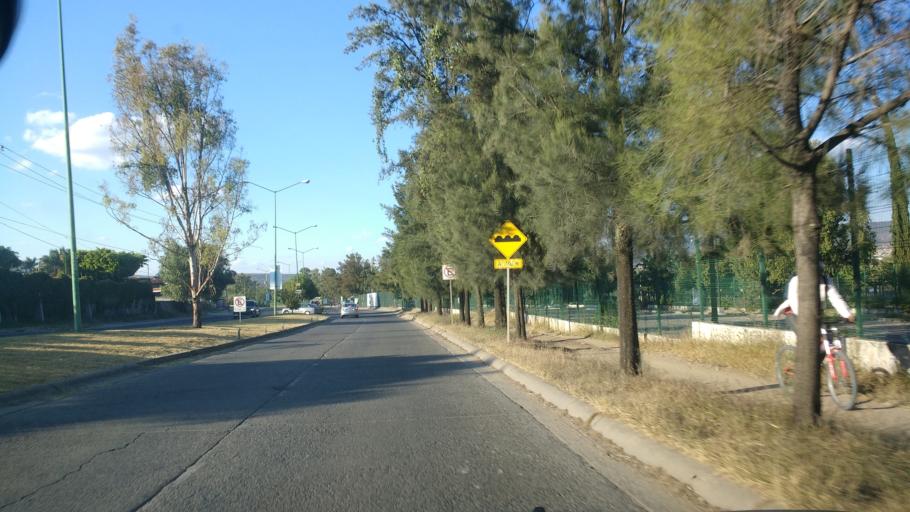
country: MX
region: Guanajuato
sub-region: Leon
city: La Ermita
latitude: 21.1730
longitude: -101.6983
